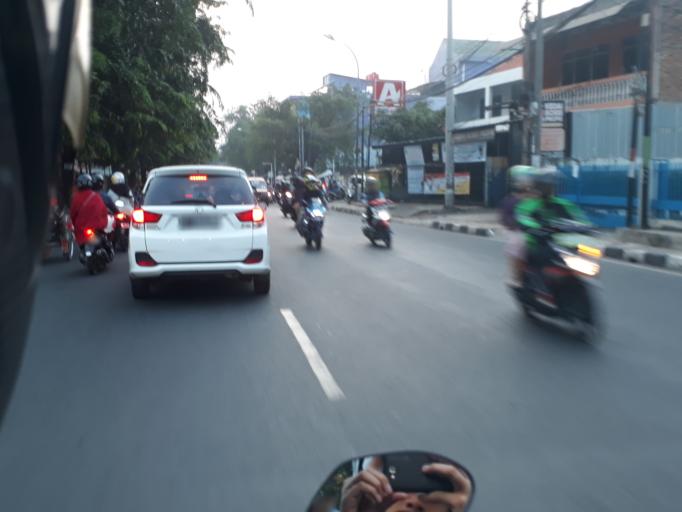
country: ID
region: West Java
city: Bekasi
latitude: -6.2451
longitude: 107.0075
